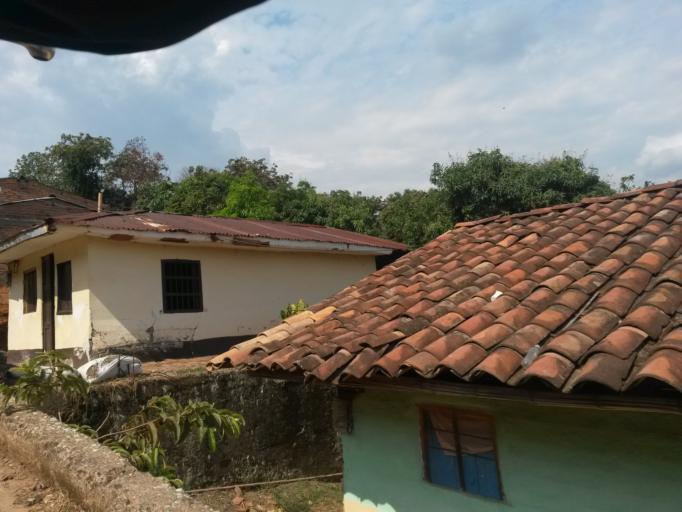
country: CO
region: Cauca
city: Buenos Aires
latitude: 3.0173
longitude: -76.6436
